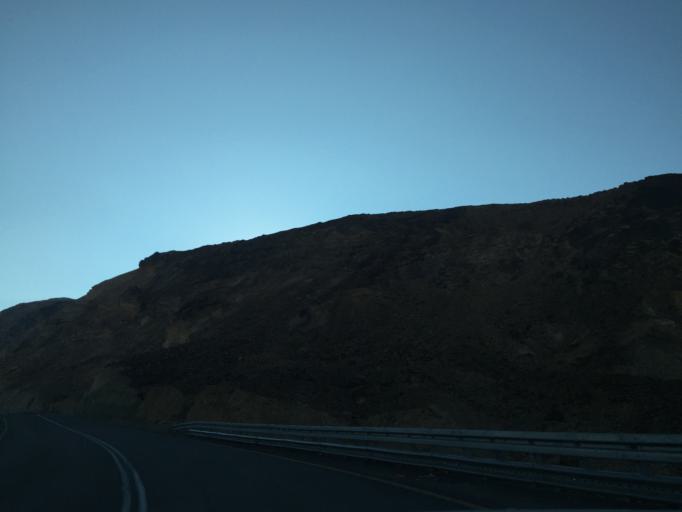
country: IL
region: Southern District
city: Mitzpe Ramon
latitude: 30.3215
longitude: 34.9564
